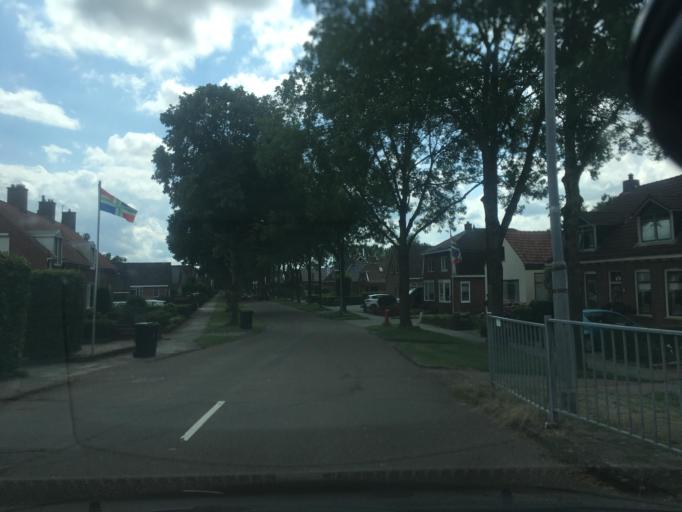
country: NL
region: Groningen
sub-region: Gemeente Hoogezand-Sappemeer
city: Sappemeer
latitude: 53.1592
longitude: 6.7866
